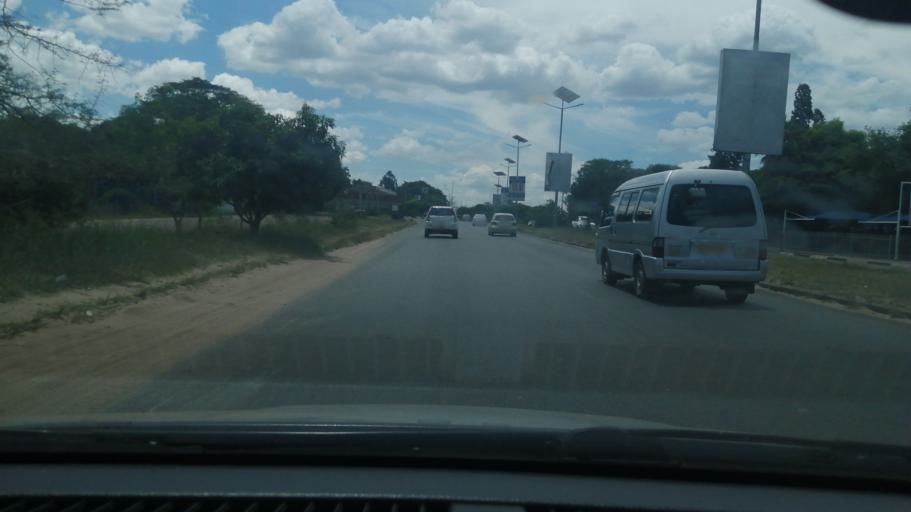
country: ZW
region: Harare
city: Harare
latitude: -17.8363
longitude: 31.1064
